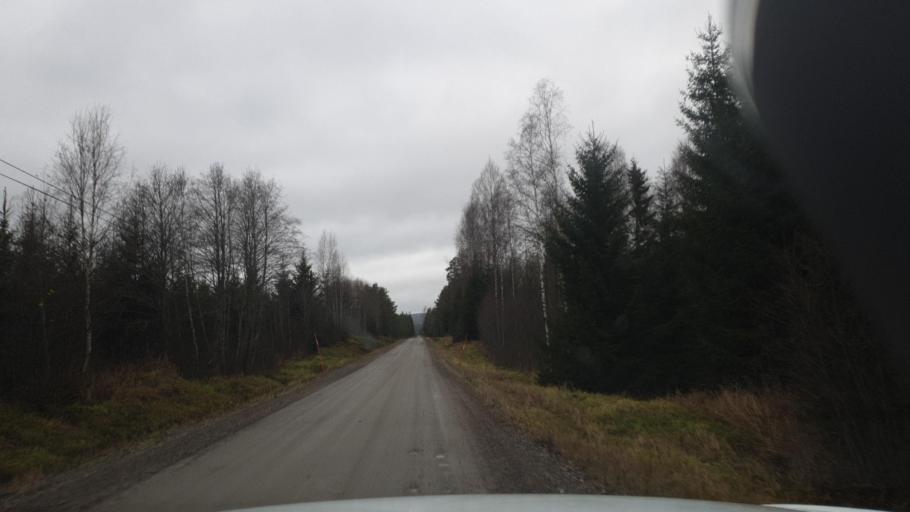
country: SE
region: Vaermland
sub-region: Eda Kommun
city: Charlottenberg
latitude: 59.9520
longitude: 12.5157
